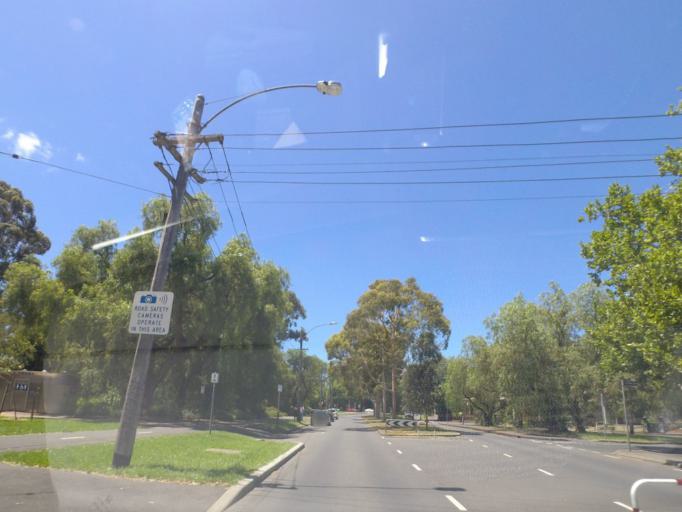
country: AU
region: Victoria
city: Parkville
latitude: -37.7927
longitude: 144.9566
